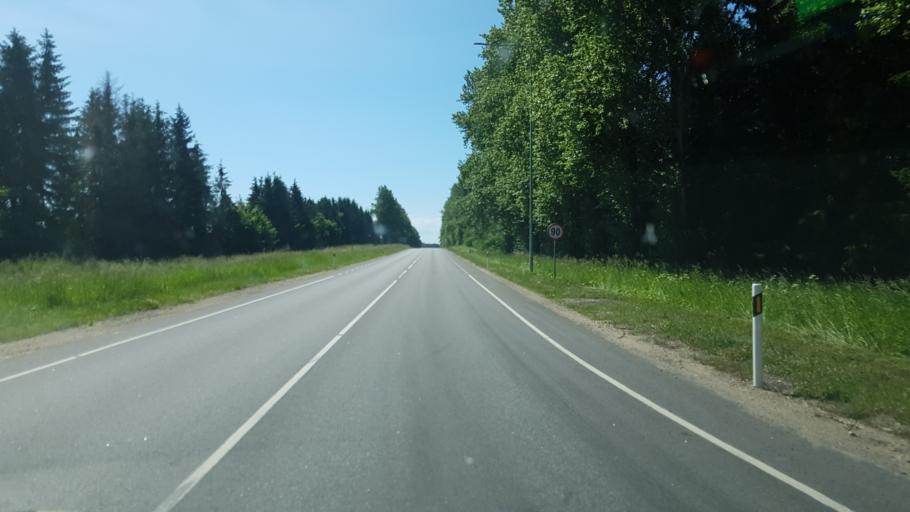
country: EE
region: Polvamaa
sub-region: Polva linn
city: Polva
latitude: 58.2804
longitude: 27.0022
